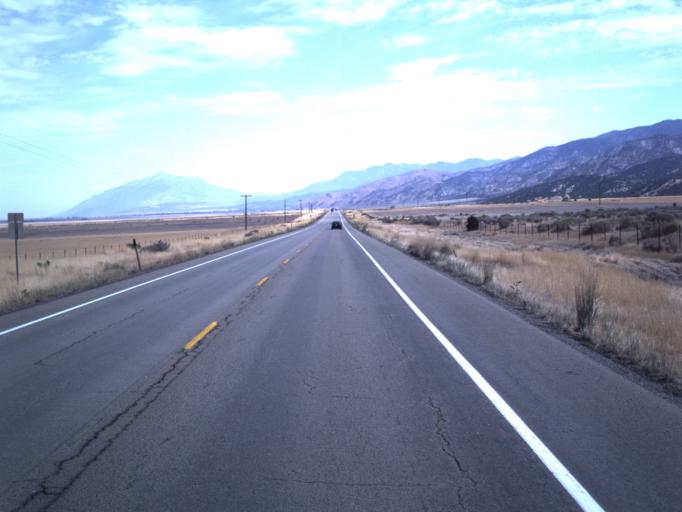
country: US
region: Utah
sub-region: Juab County
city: Nephi
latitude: 39.4575
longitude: -111.9050
